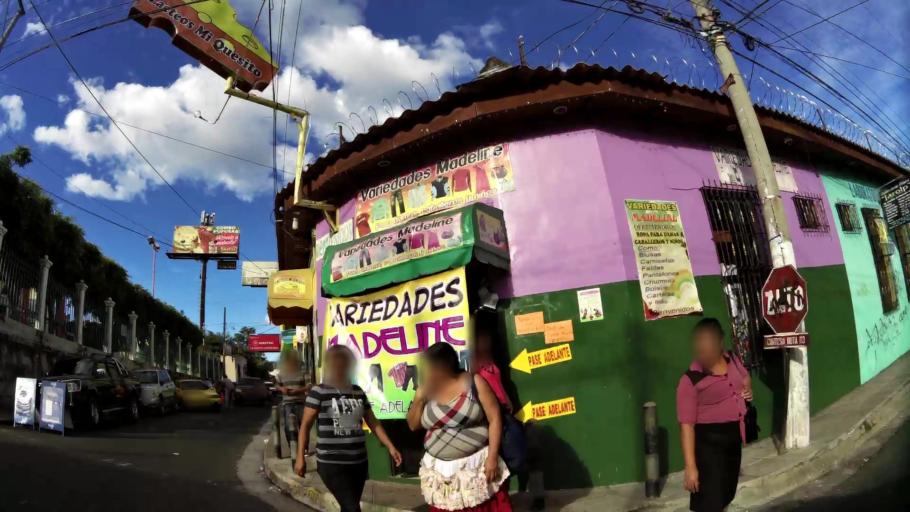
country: SV
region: Cuscatlan
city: Cojutepeque
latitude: 13.7214
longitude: -88.9337
